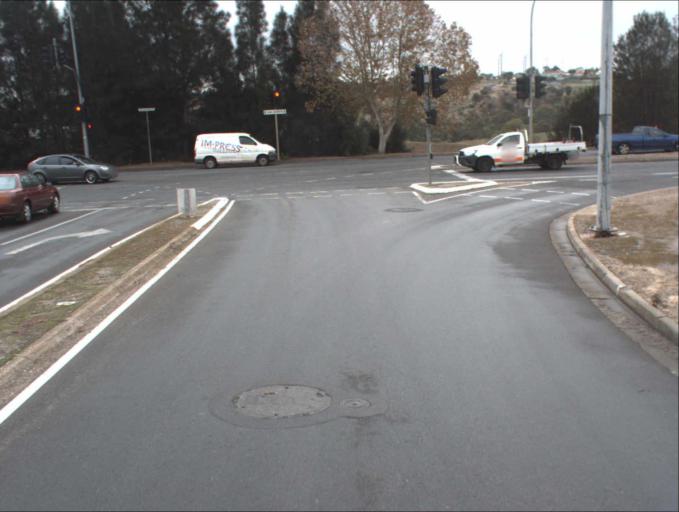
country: AU
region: South Australia
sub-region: Salisbury
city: Ingle Farm
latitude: -34.8472
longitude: 138.6354
